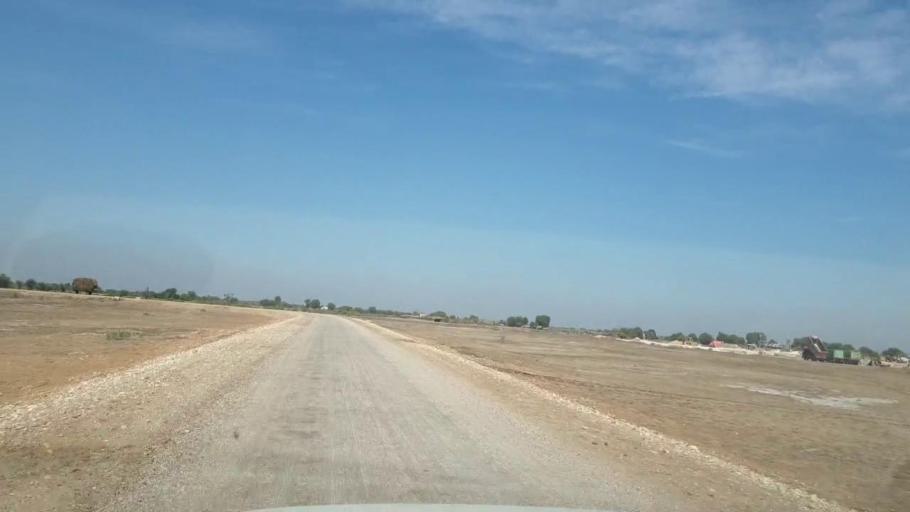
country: PK
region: Sindh
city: Mirpur Khas
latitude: 25.6481
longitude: 69.1917
